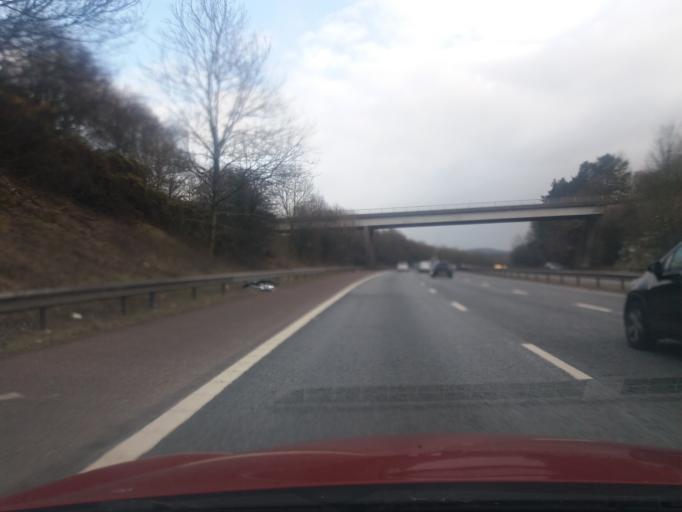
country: GB
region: England
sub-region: Lancashire
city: Clayton-le-Woods
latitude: 53.6955
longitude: -2.6272
